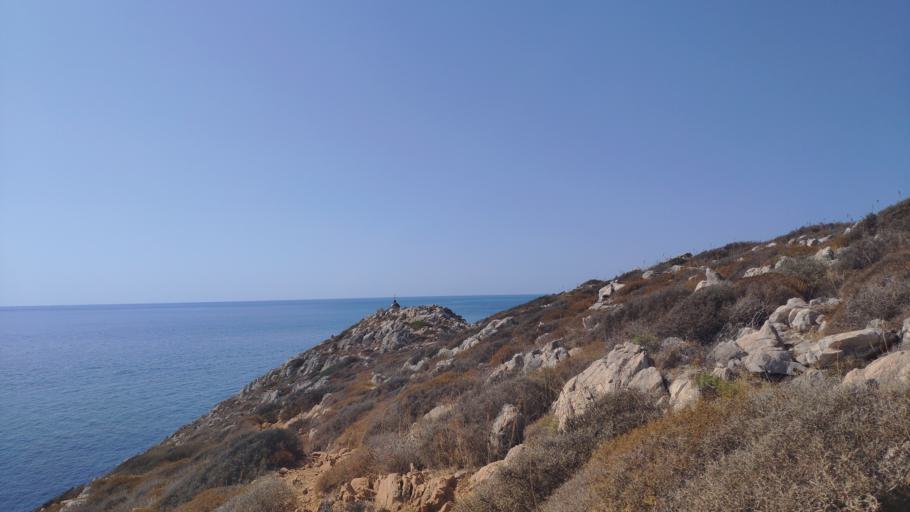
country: GR
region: Peloponnese
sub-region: Nomos Lakonias
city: Gytheio
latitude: 36.3877
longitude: 22.4828
